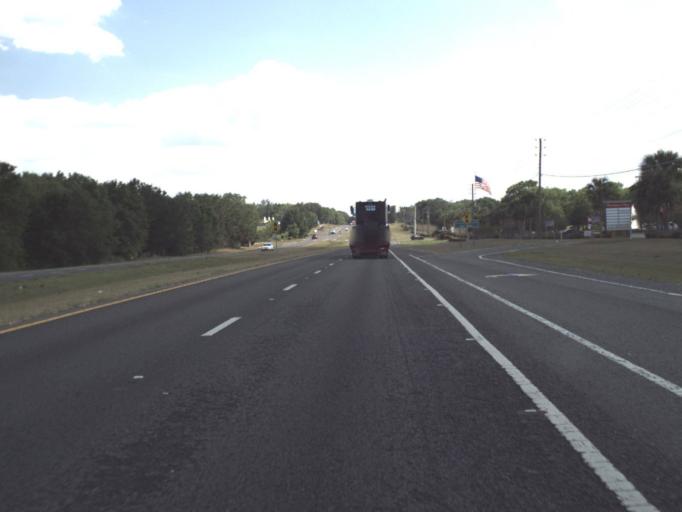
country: US
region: Florida
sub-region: Lake County
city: Hawthorne
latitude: 28.7172
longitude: -81.8614
